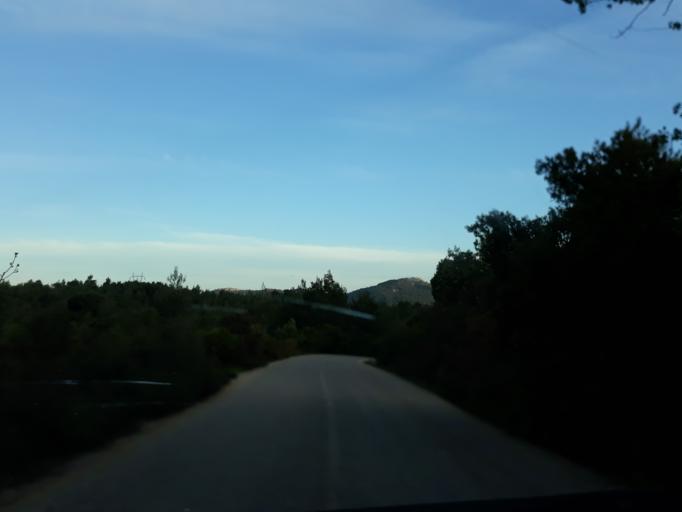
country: GR
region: Attica
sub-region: Nomarchia Anatolikis Attikis
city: Afidnes
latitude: 38.2062
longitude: 23.7886
